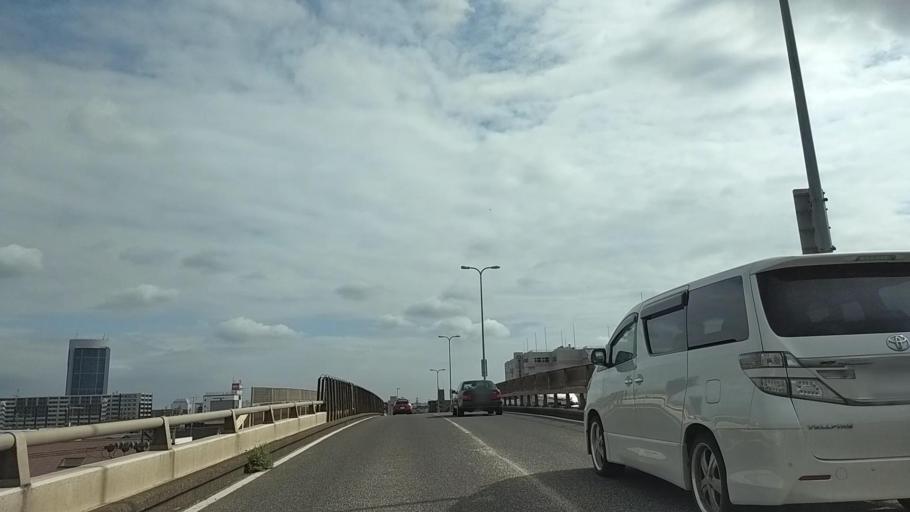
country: JP
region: Kanagawa
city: Atsugi
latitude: 35.4324
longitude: 139.3569
